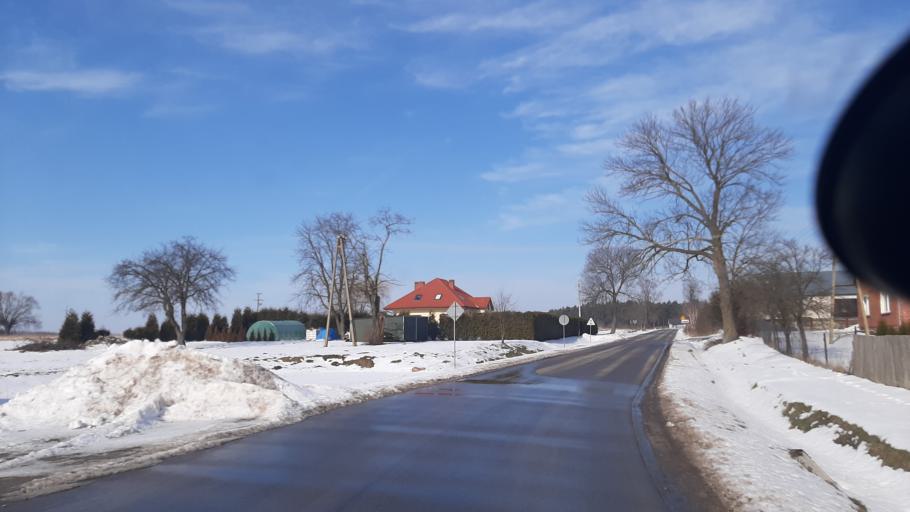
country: PL
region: Lublin Voivodeship
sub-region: Powiat pulawski
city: Baranow
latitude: 51.5389
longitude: 22.1486
